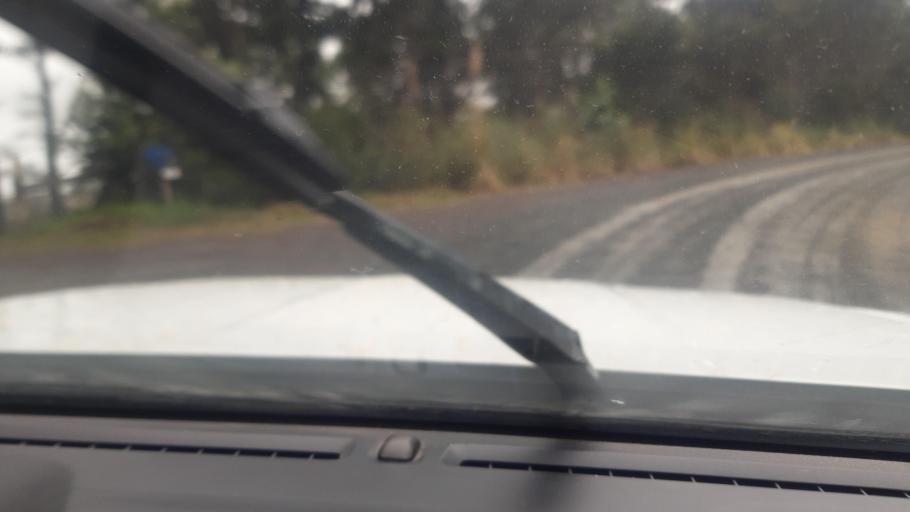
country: NZ
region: Northland
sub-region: Far North District
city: Kaitaia
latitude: -34.9861
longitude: 173.2131
